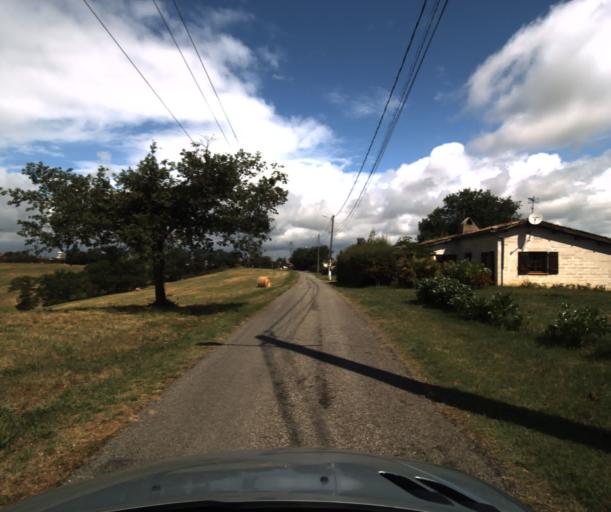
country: FR
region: Midi-Pyrenees
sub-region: Departement du Tarn-et-Garonne
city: Lavit
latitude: 43.9502
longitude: 0.9250
